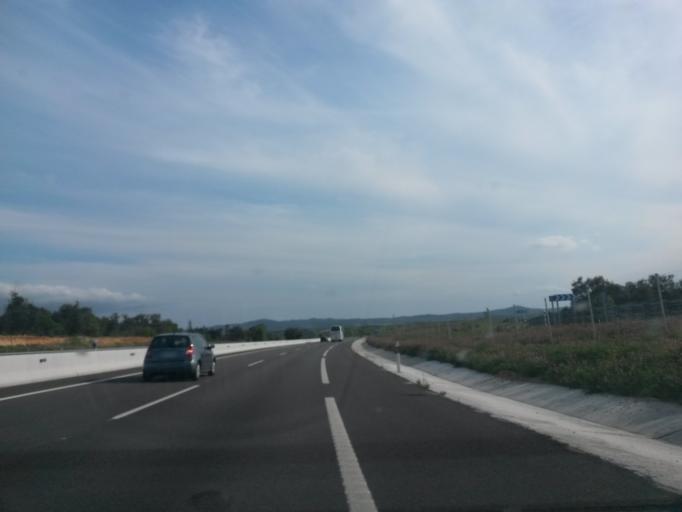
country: ES
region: Catalonia
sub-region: Provincia de Girona
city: Sils
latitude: 41.8247
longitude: 2.7631
